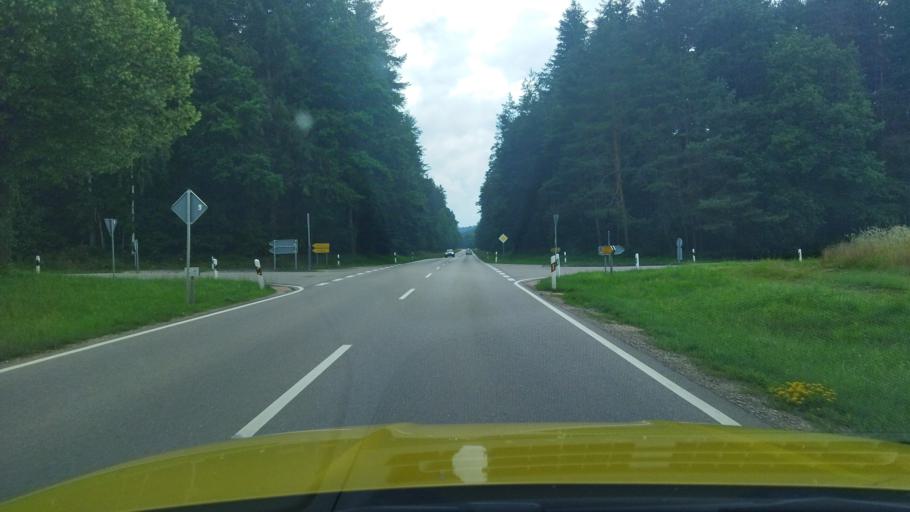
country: DE
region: Bavaria
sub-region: Regierungsbezirk Mittelfranken
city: Pleinfeld
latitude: 49.1046
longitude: 10.9476
